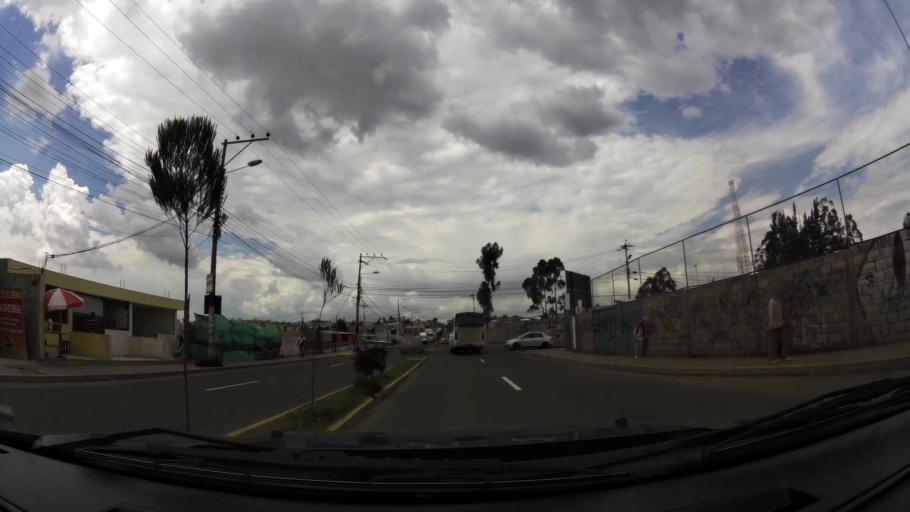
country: EC
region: Pichincha
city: Quito
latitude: -0.0999
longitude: -78.4460
